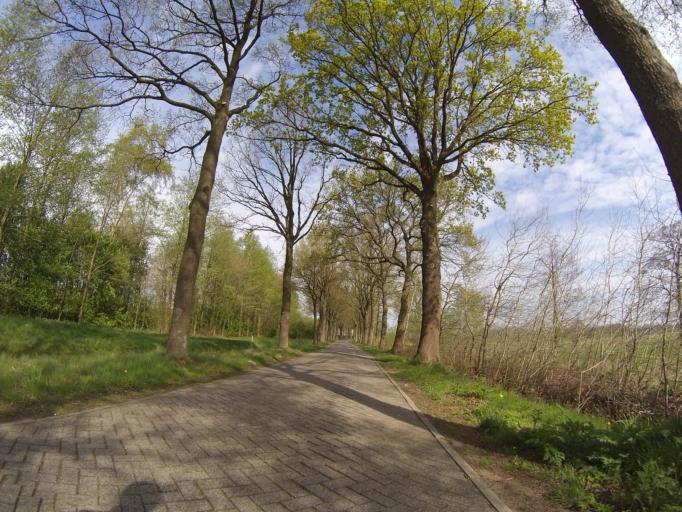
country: NL
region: Drenthe
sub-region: Gemeente Coevorden
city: Sleen
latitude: 52.8025
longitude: 6.7081
